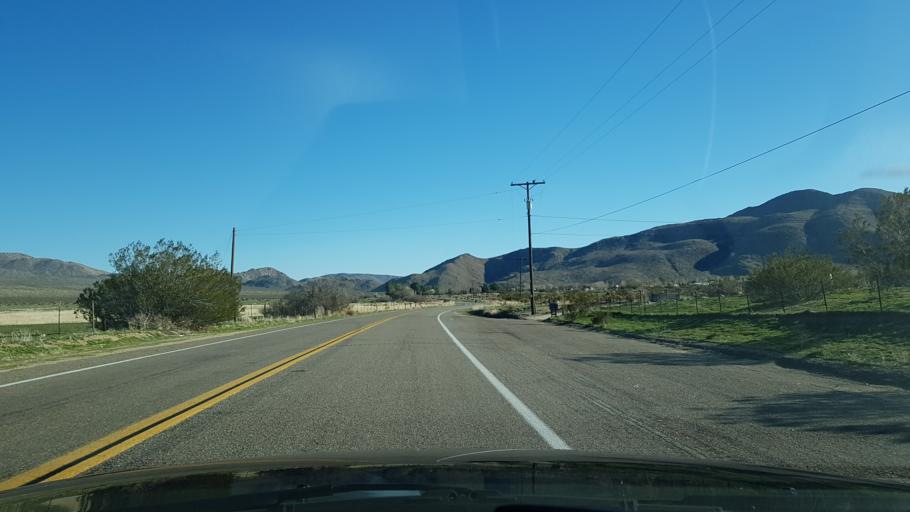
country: US
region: California
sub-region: San Diego County
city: Julian
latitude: 33.0662
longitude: -116.4285
